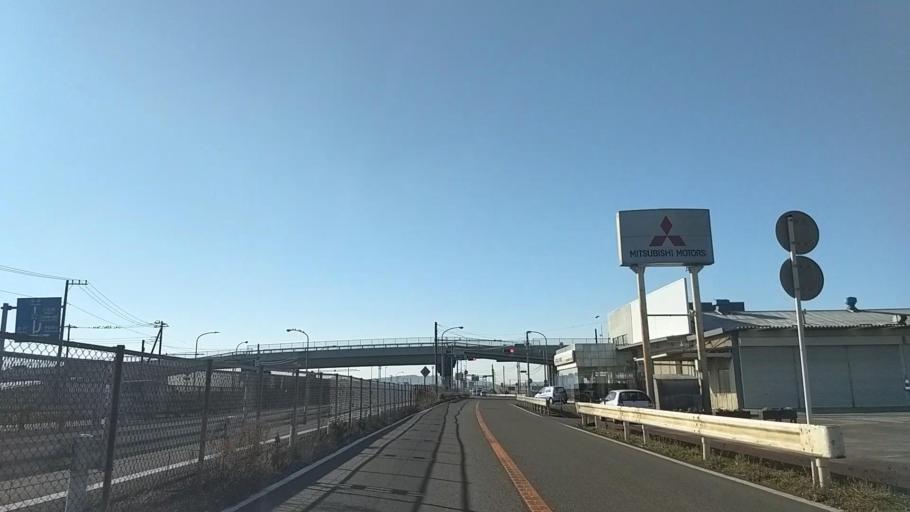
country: JP
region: Kanagawa
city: Isehara
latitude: 35.3871
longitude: 139.3317
